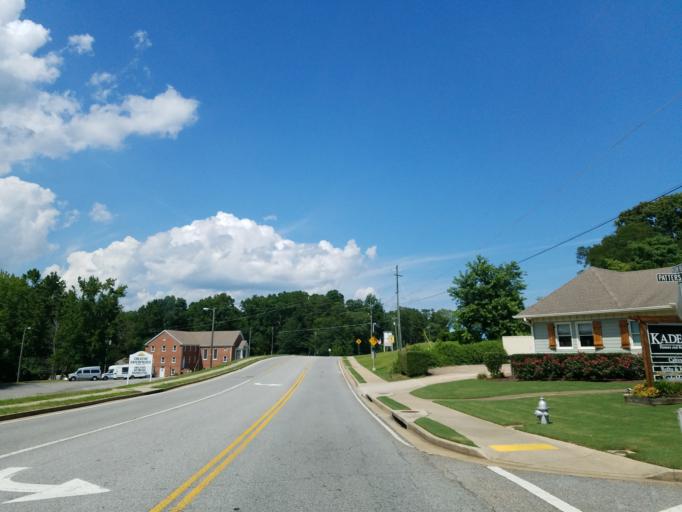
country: US
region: Georgia
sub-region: Forsyth County
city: Cumming
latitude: 34.2096
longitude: -84.1347
